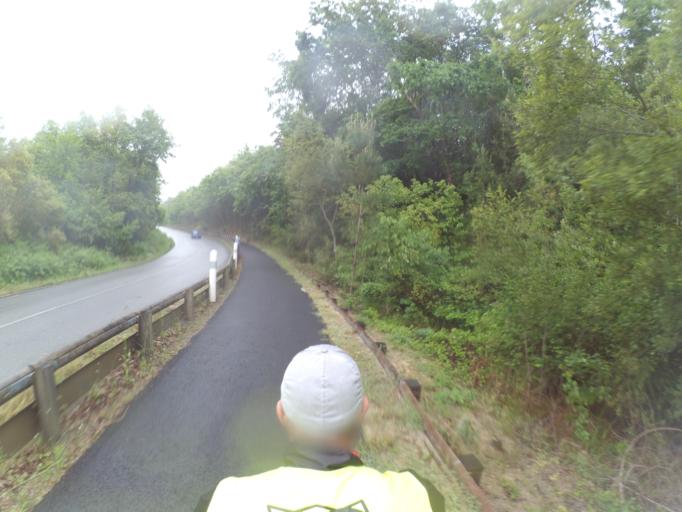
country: FR
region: Aquitaine
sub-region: Departement des Landes
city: Mimizan
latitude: 44.2337
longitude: -1.2237
